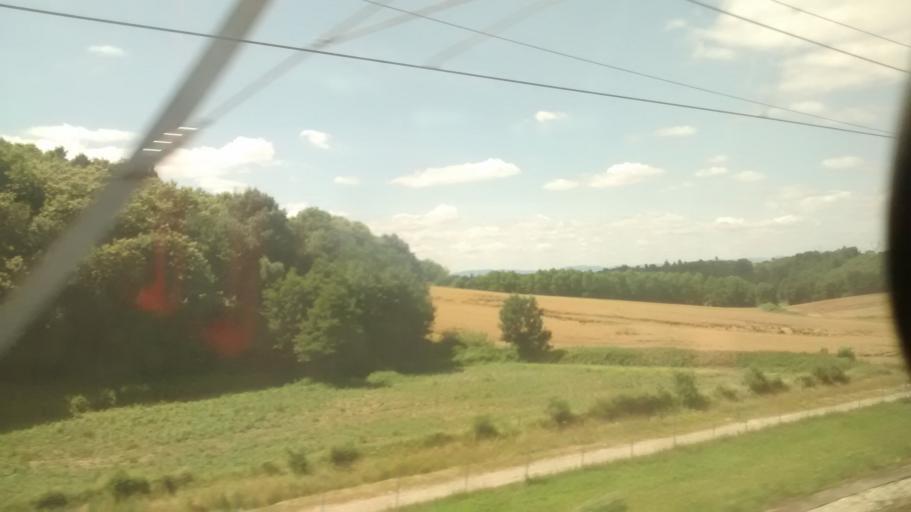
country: FR
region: Rhone-Alpes
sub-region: Departement du Rhone
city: Montanay
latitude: 45.8862
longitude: 4.8789
